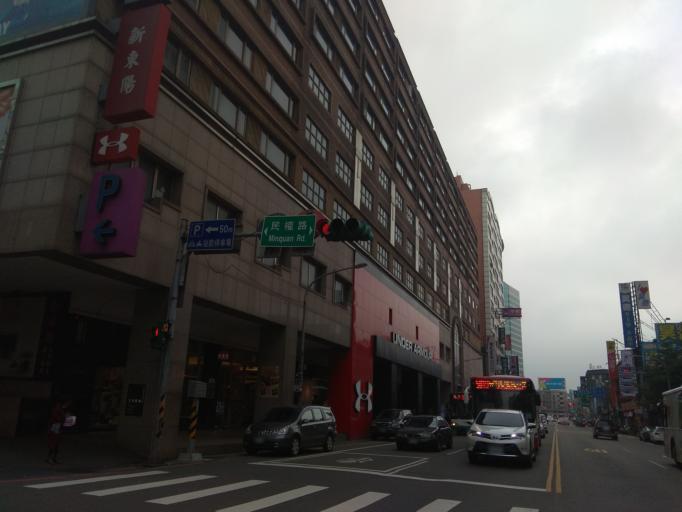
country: TW
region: Taiwan
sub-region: Taoyuan
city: Taoyuan
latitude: 24.9900
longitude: 121.3117
